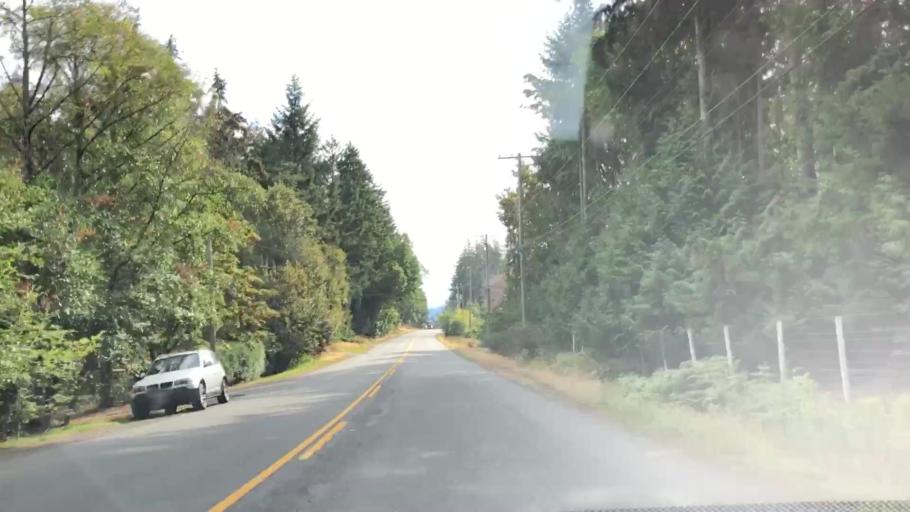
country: CA
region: British Columbia
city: North Saanich
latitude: 48.6865
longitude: -123.5600
